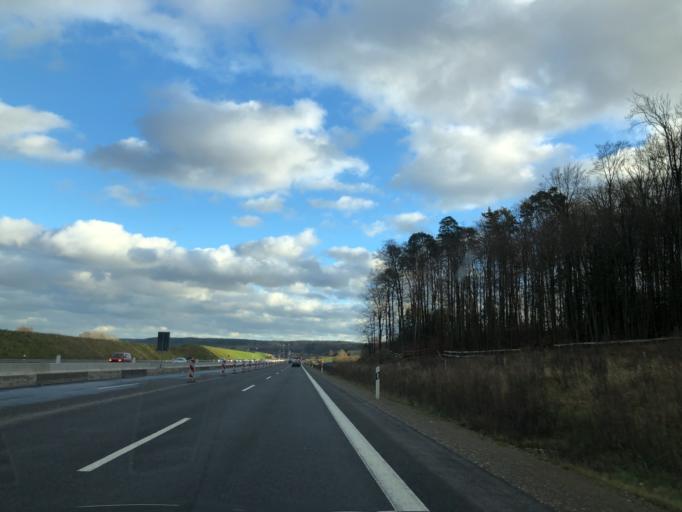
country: DE
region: Bavaria
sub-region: Regierungsbezirk Unterfranken
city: Geiselwind
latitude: 49.7799
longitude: 10.4484
